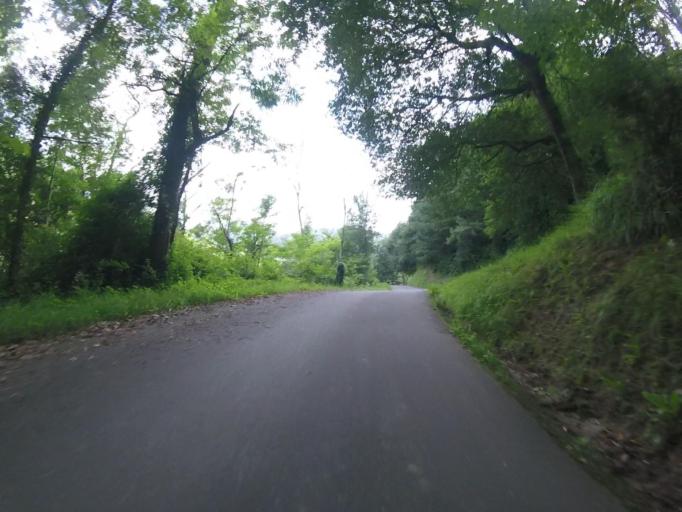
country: ES
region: Basque Country
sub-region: Provincia de Guipuzcoa
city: Hernani
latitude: 43.2501
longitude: -1.9511
